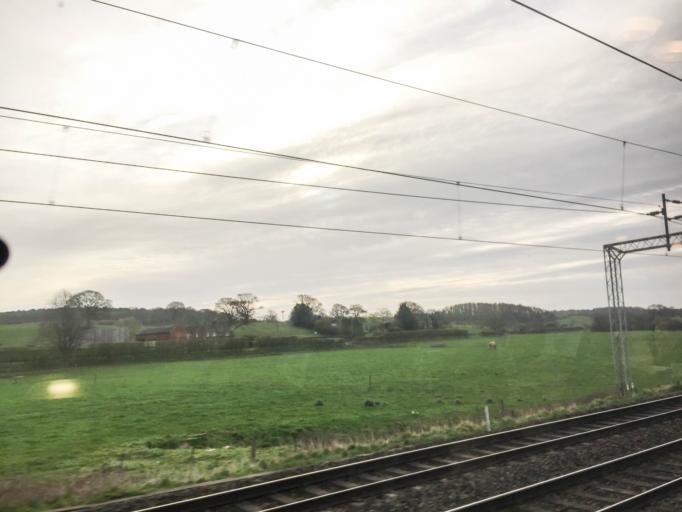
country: GB
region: England
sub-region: Staffordshire
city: Standon
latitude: 52.9400
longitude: -2.2707
